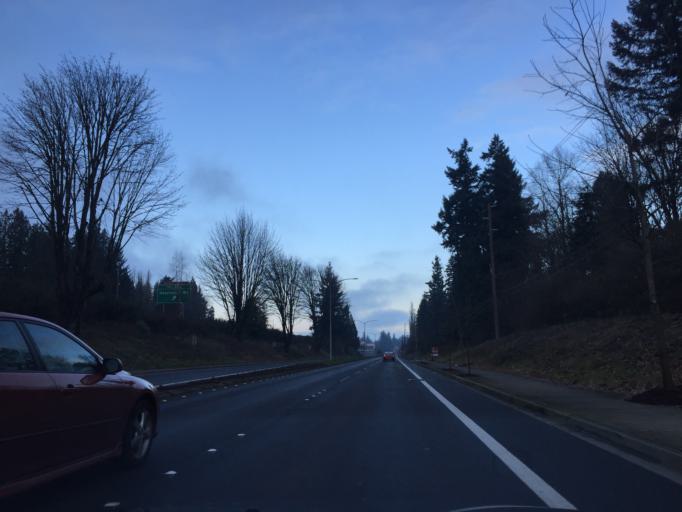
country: US
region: Washington
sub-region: Thurston County
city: Tumwater
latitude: 47.0073
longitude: -122.9073
